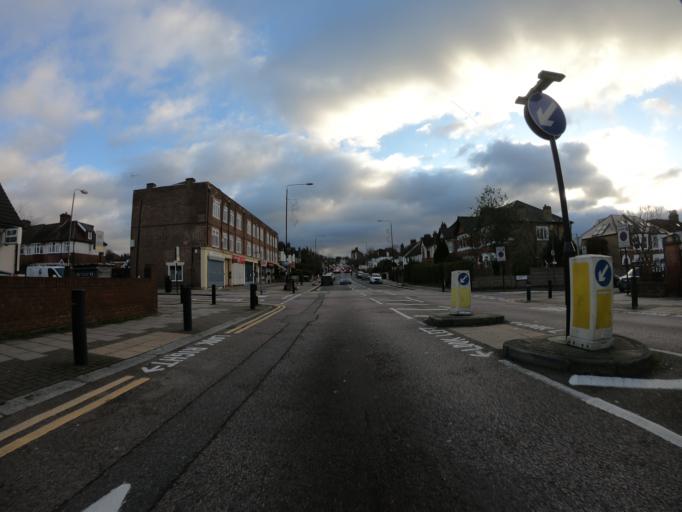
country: GB
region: England
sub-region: Greater London
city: Woolwich
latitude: 51.4588
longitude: 0.0587
